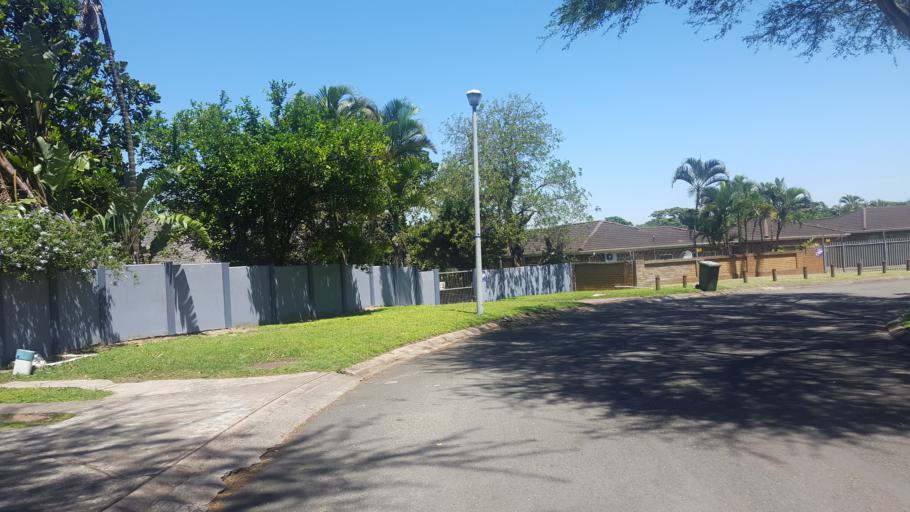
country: ZA
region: KwaZulu-Natal
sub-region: uThungulu District Municipality
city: Richards Bay
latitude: -28.7658
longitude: 32.0641
